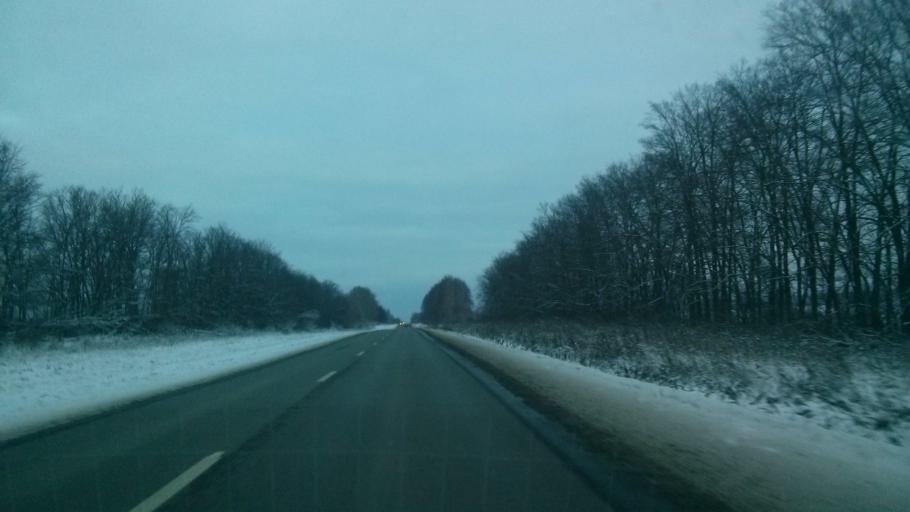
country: RU
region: Nizjnij Novgorod
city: Bogorodsk
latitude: 56.0532
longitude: 43.4068
